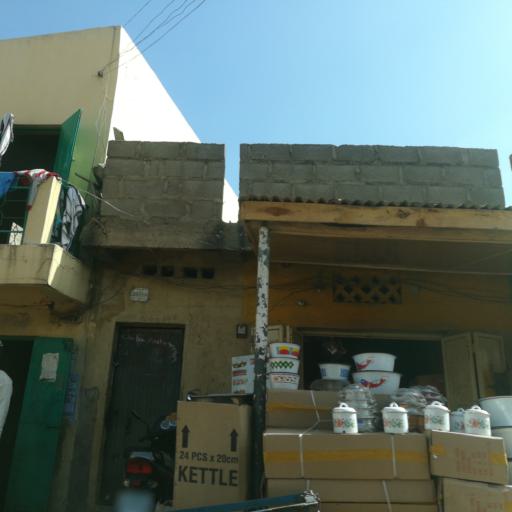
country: NG
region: Kano
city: Kano
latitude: 12.0042
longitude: 8.5163
